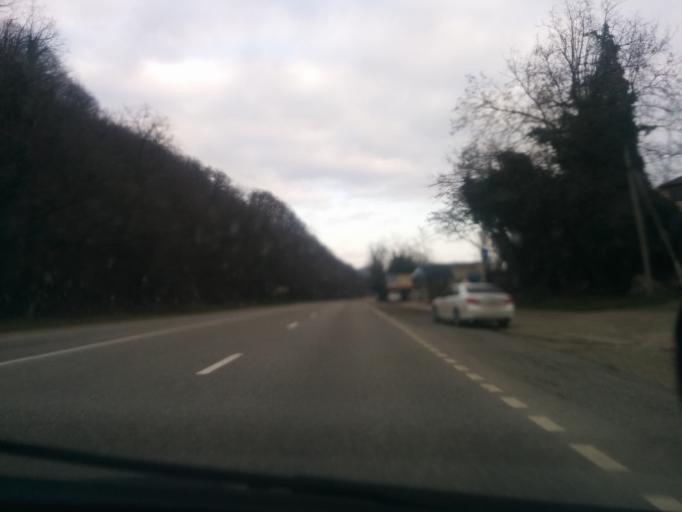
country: RU
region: Krasnodarskiy
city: Nebug
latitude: 44.1694
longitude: 38.9849
